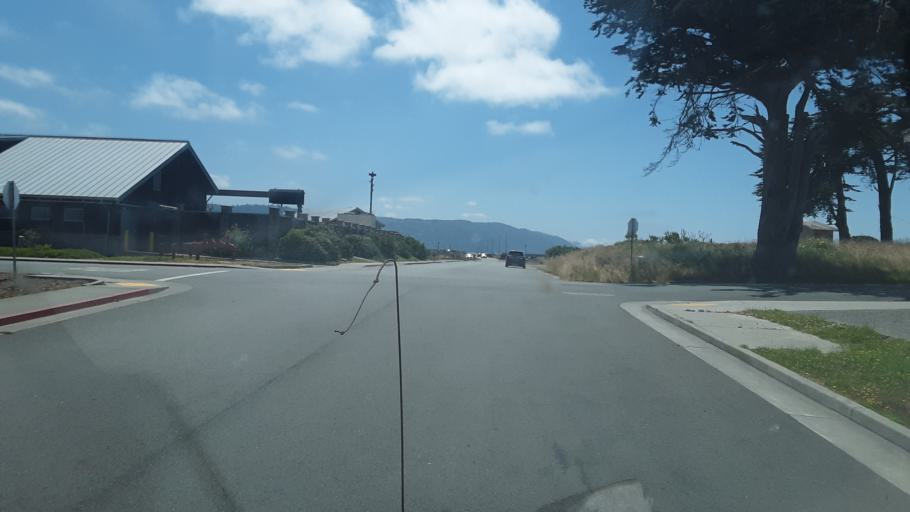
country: US
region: California
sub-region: Del Norte County
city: Crescent City
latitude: 41.7475
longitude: -124.2016
